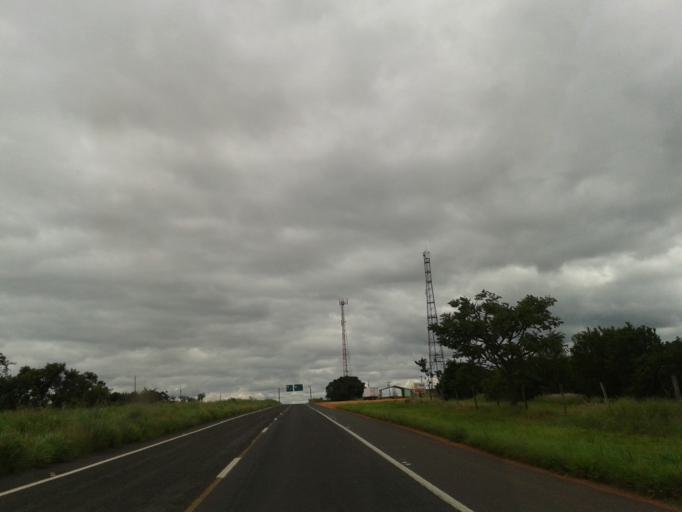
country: BR
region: Minas Gerais
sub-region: Monte Alegre De Minas
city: Monte Alegre de Minas
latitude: -18.8801
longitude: -49.0038
